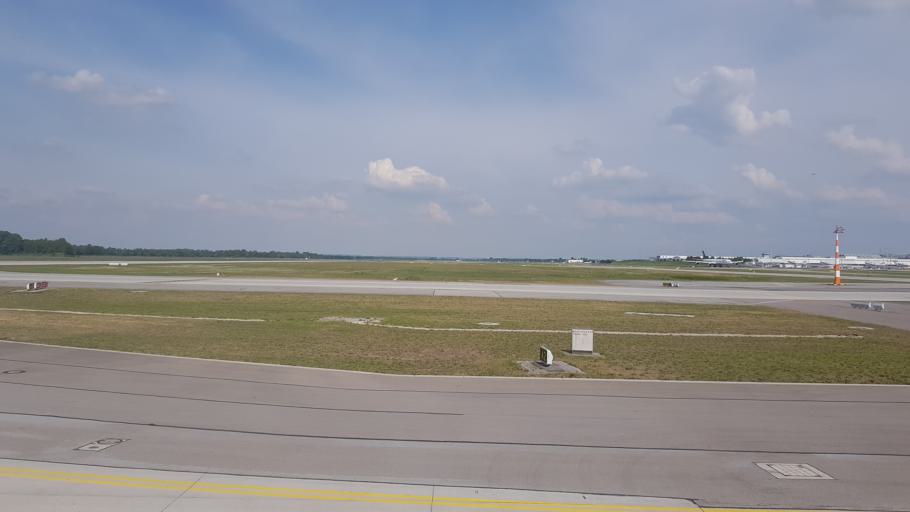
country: DE
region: Bavaria
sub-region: Upper Bavaria
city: Hallbergmoos
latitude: 48.3615
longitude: 11.7680
